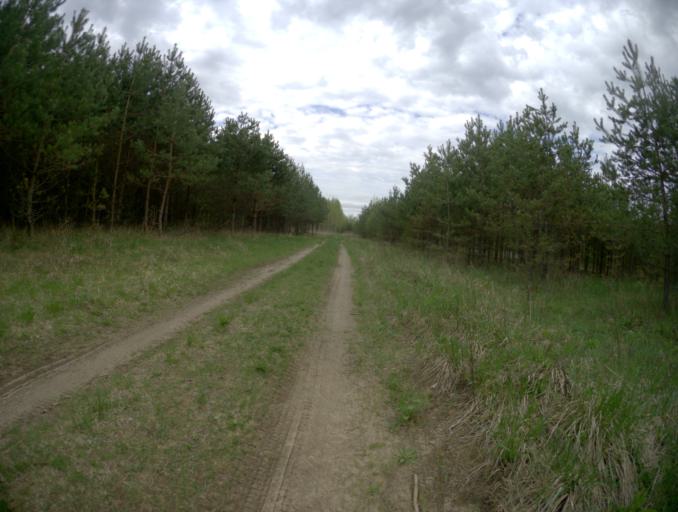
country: RU
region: Vladimir
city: Golovino
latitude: 55.9321
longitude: 40.3946
